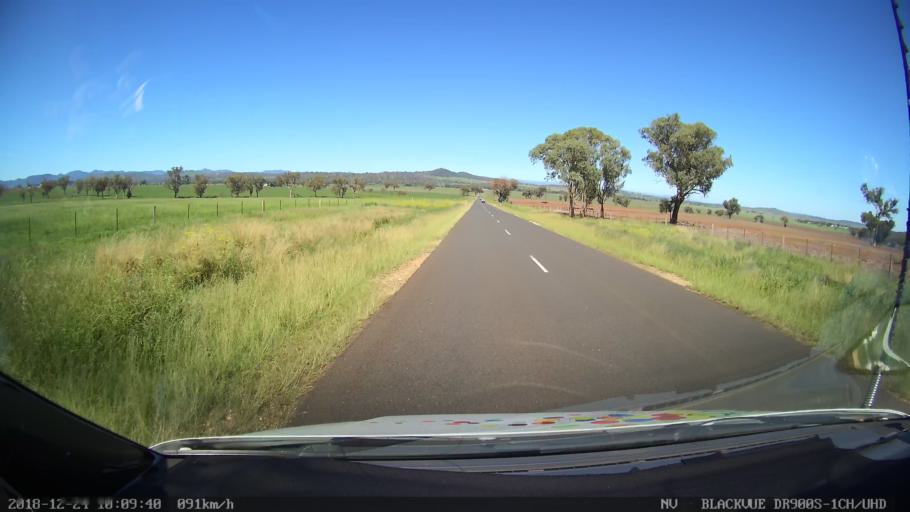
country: AU
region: New South Wales
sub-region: Liverpool Plains
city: Quirindi
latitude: -31.6646
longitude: 150.6872
